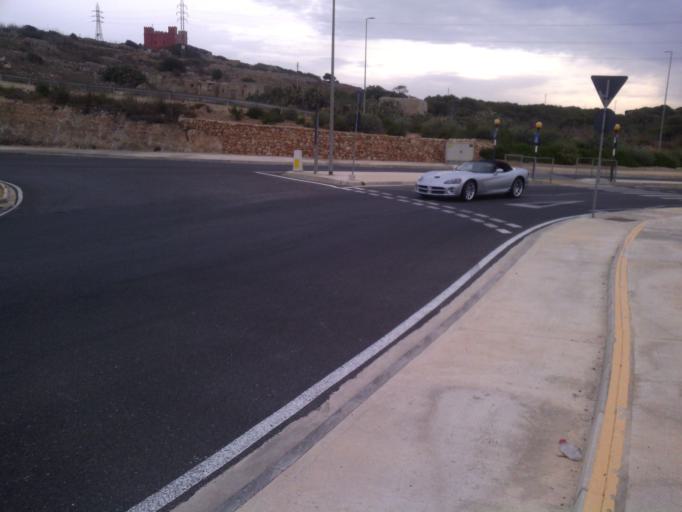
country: MT
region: Il-Mellieha
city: Mellieha
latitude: 35.9767
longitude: 14.3466
